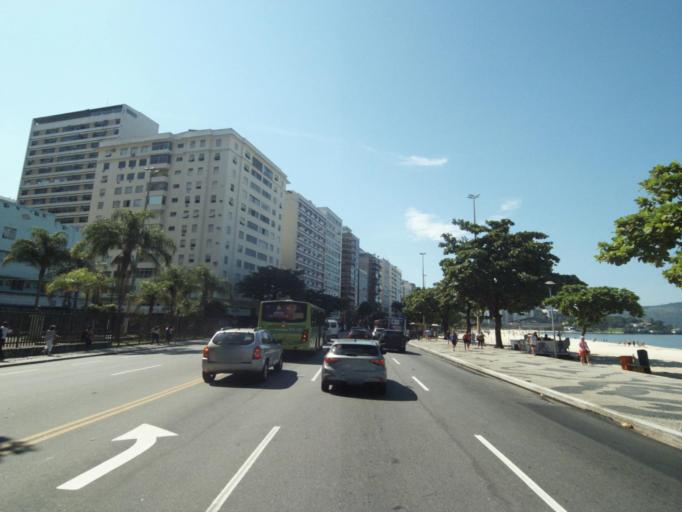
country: BR
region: Rio de Janeiro
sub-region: Niteroi
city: Niteroi
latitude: -22.9044
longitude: -43.1157
